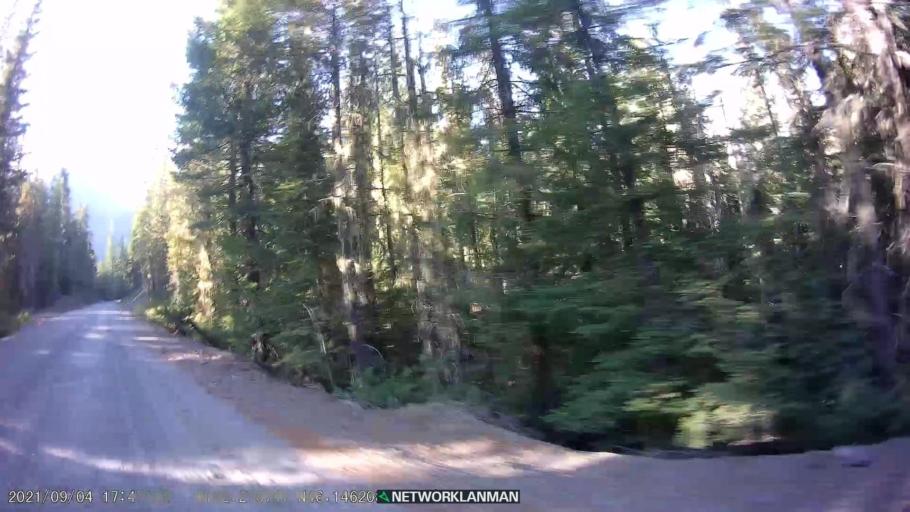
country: US
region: Washington
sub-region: Clark County
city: Amboy
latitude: 46.1463
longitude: -122.2738
